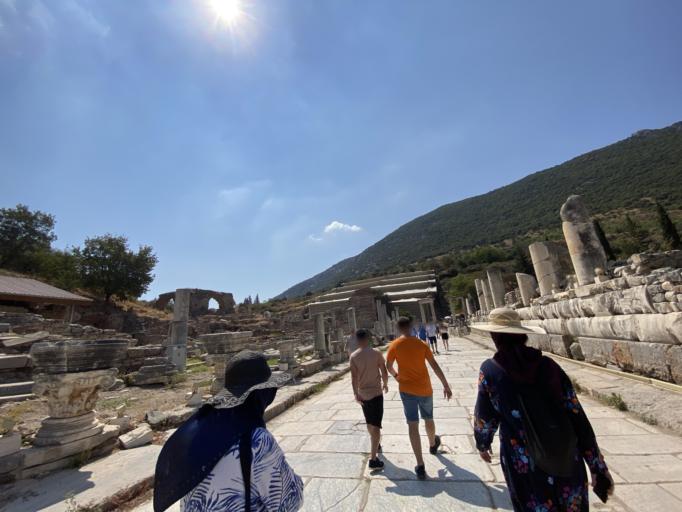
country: TR
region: Izmir
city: Selcuk
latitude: 37.9395
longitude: 27.3415
